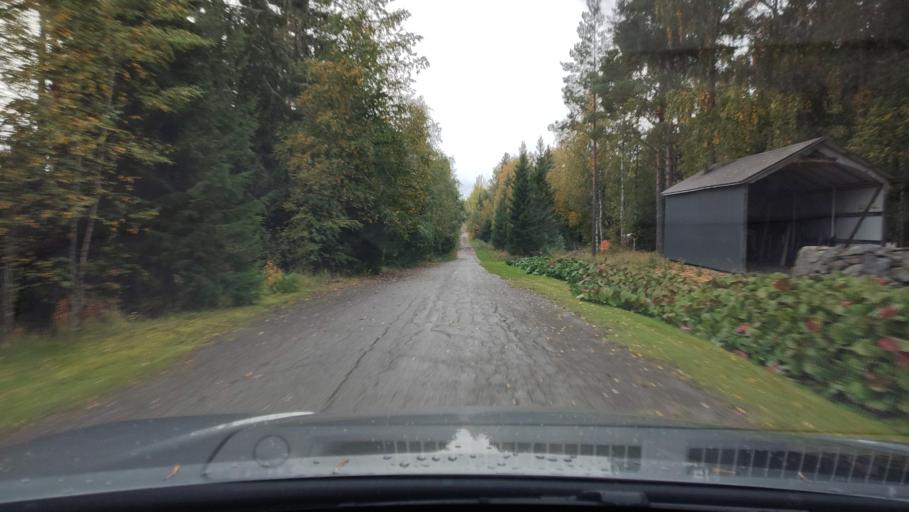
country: FI
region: Ostrobothnia
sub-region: Sydosterbotten
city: Kristinestad
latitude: 62.2656
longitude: 21.4620
